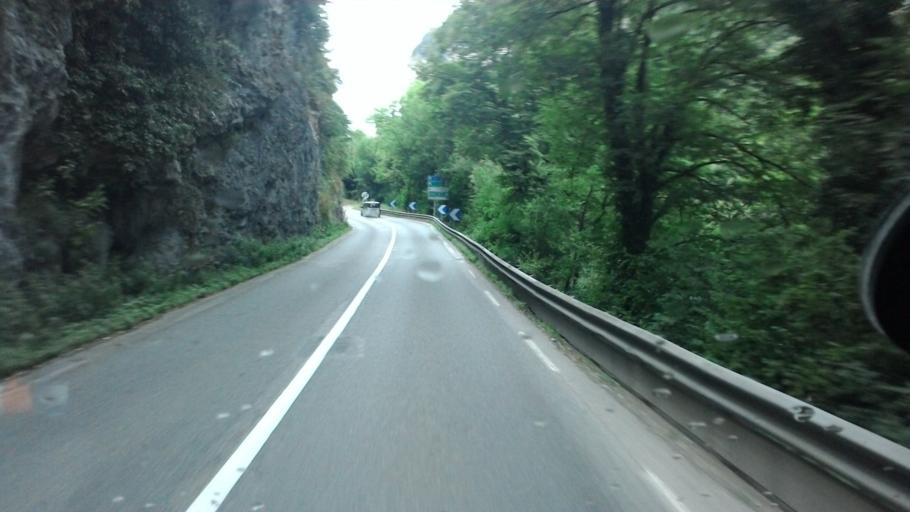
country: FR
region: Rhone-Alpes
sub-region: Departement de la Savoie
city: Yenne
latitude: 45.7094
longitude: 5.7311
